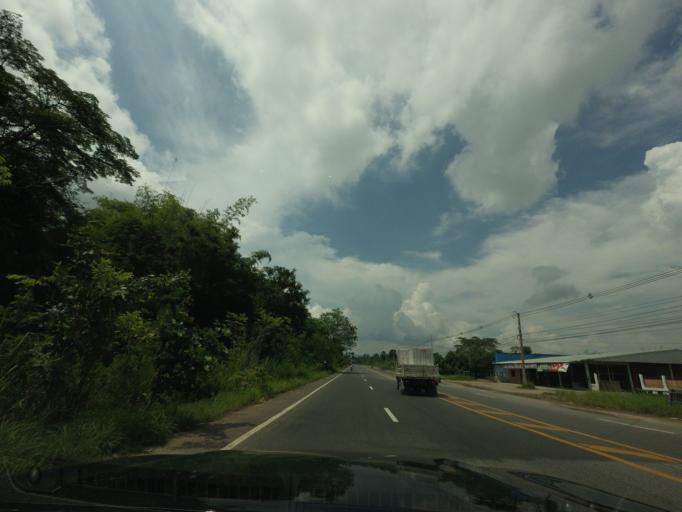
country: TH
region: Khon Kaen
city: Wiang Kao
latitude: 16.6766
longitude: 102.3306
